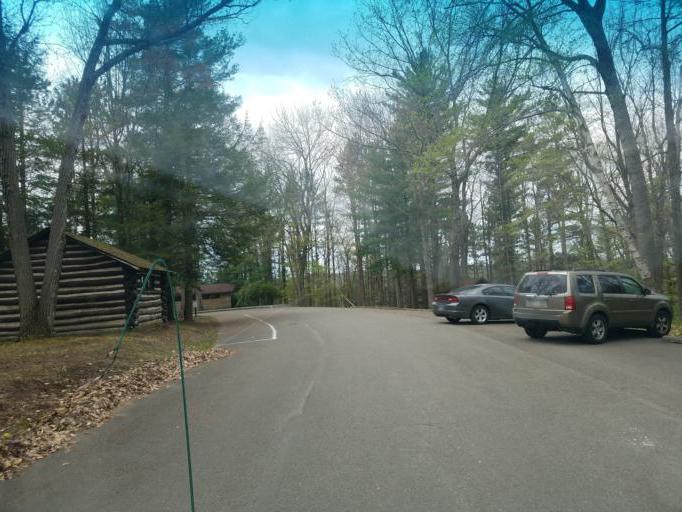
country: US
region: Pennsylvania
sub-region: Tioga County
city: Wellsboro
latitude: 41.6971
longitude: -77.4539
